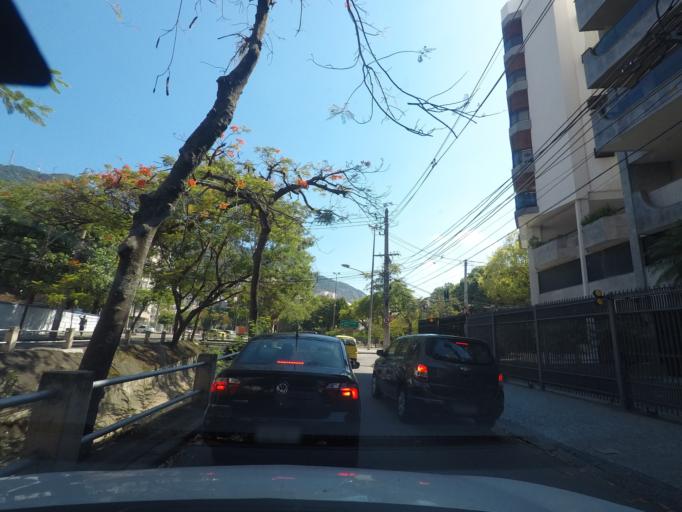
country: BR
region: Rio de Janeiro
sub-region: Rio De Janeiro
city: Rio de Janeiro
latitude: -22.9312
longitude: -43.2426
